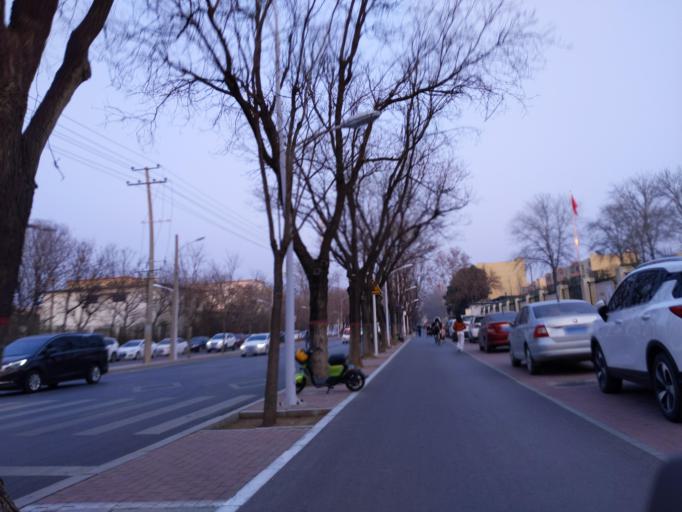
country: CN
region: Henan Sheng
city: Zhongyuanlu
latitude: 35.7696
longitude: 115.0924
